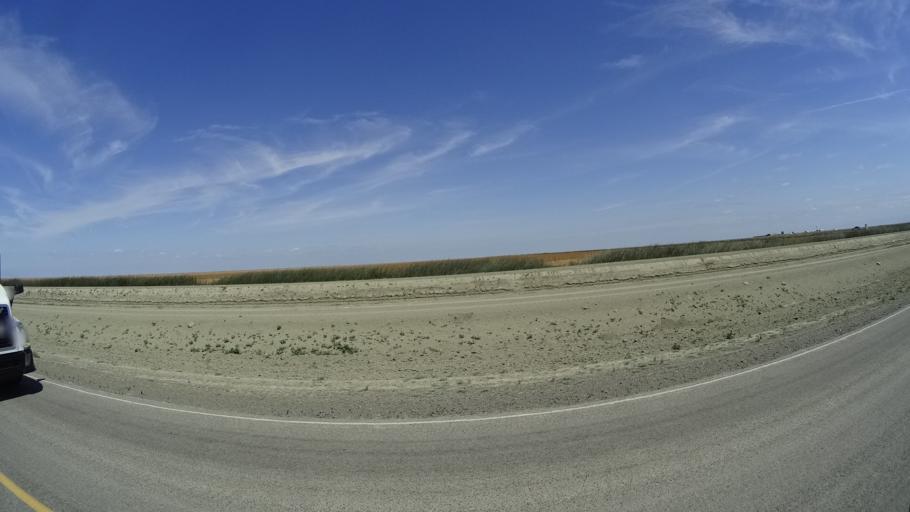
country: US
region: California
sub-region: Tulare County
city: Alpaugh
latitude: 35.9344
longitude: -119.6109
